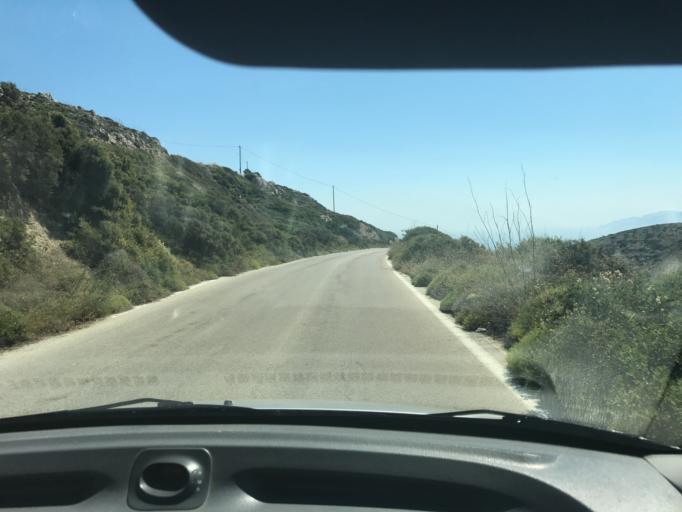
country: GR
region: South Aegean
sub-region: Nomos Dodekanisou
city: Karpathos
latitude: 35.4877
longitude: 27.1560
